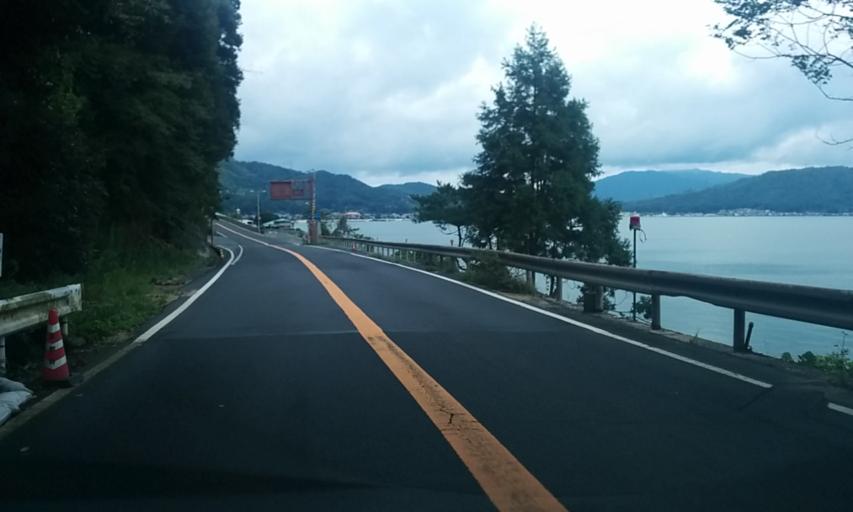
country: JP
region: Kyoto
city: Miyazu
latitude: 35.5346
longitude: 135.2514
